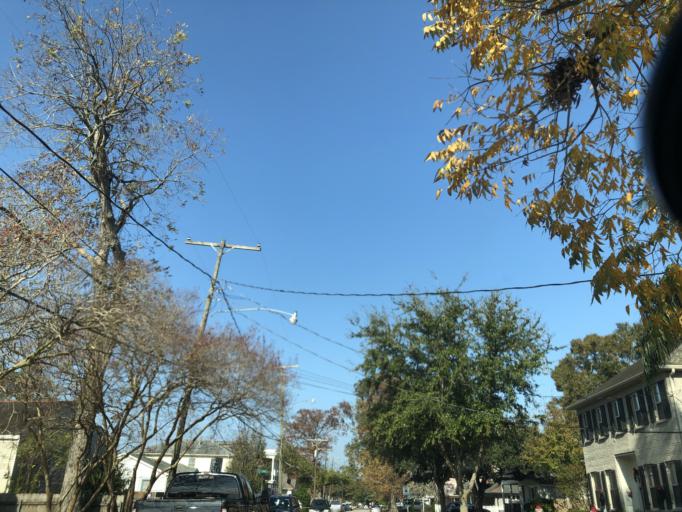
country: US
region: Louisiana
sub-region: Jefferson Parish
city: Metairie
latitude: 29.9854
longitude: -90.1526
